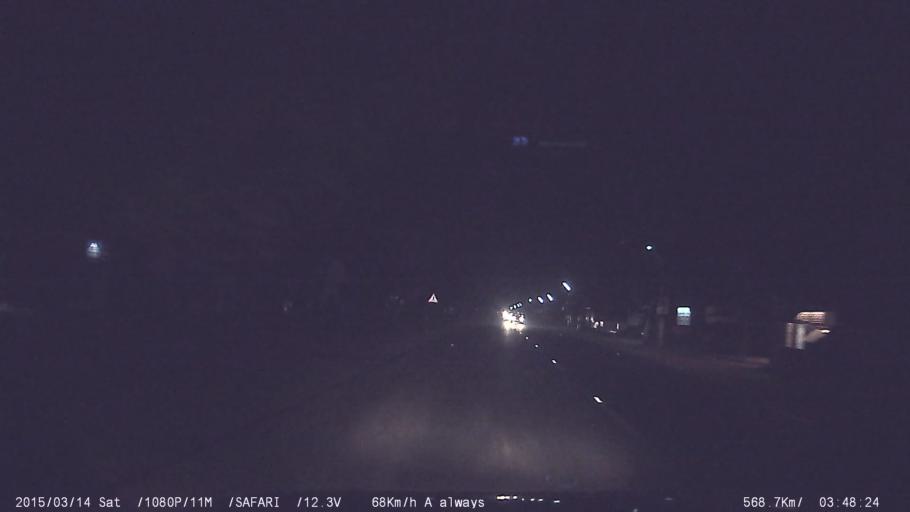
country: IN
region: Kerala
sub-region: Alappuzha
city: Alleppey
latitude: 9.5390
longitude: 76.3272
